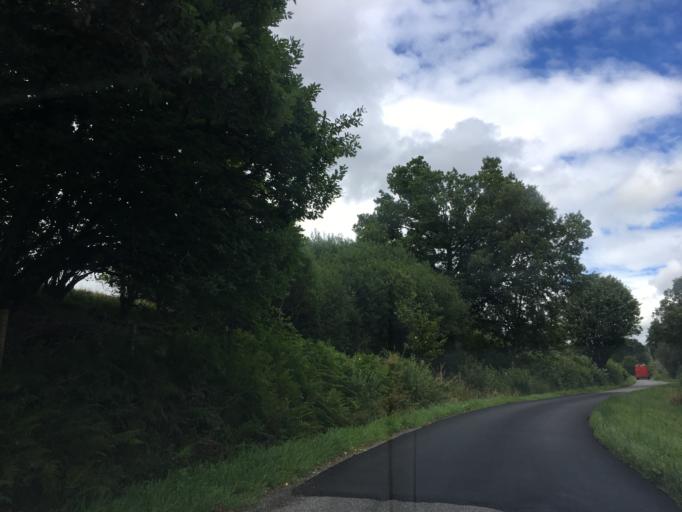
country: GB
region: Scotland
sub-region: Argyll and Bute
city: Oban
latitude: 56.3448
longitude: -5.1928
